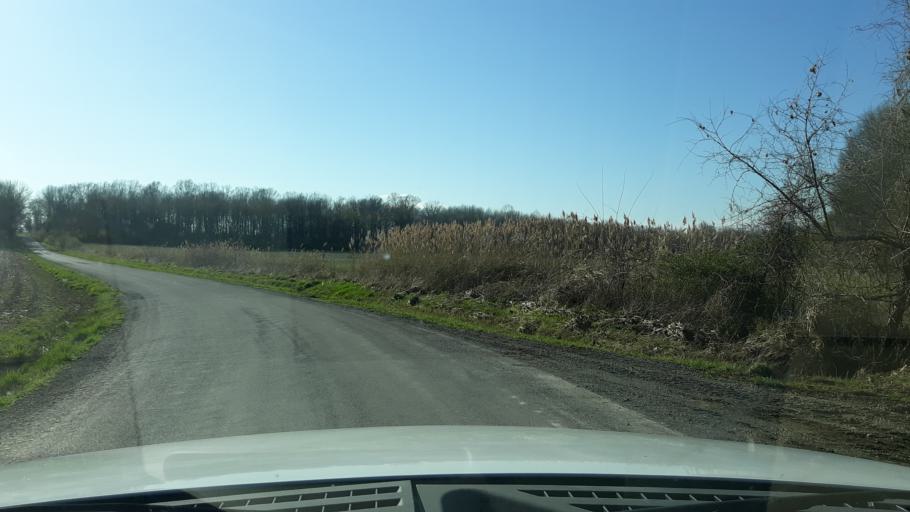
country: US
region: Illinois
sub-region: Saline County
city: Harrisburg
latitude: 37.7627
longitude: -88.5724
